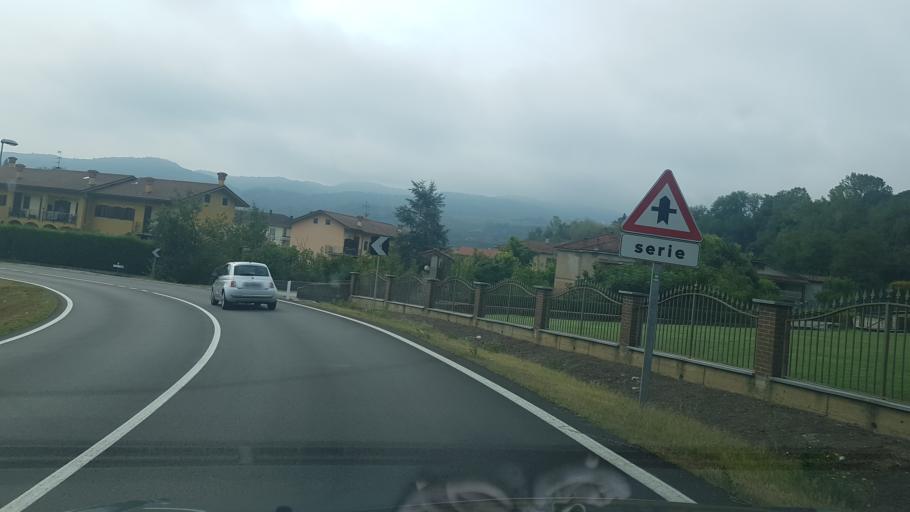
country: IT
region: Piedmont
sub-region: Provincia di Cuneo
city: Ceva
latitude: 44.3840
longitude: 8.0256
